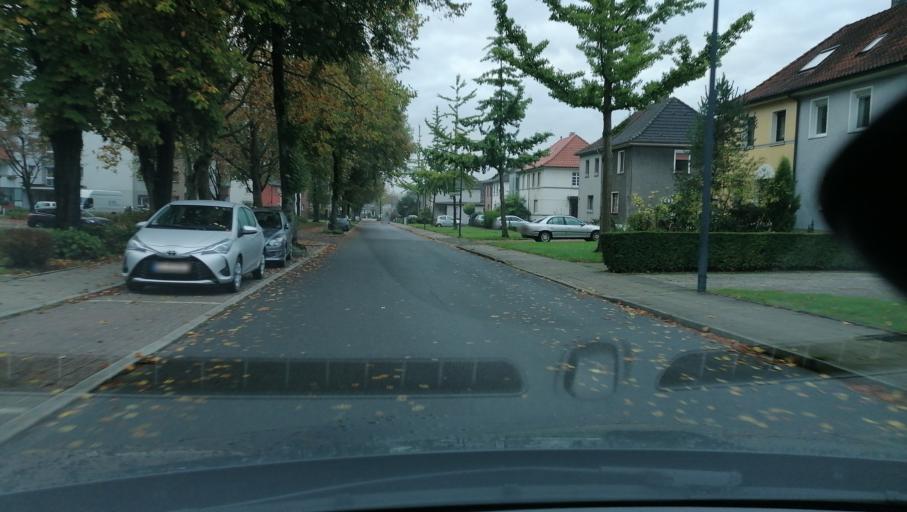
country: DE
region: North Rhine-Westphalia
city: Herten
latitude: 51.5878
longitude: 7.1371
